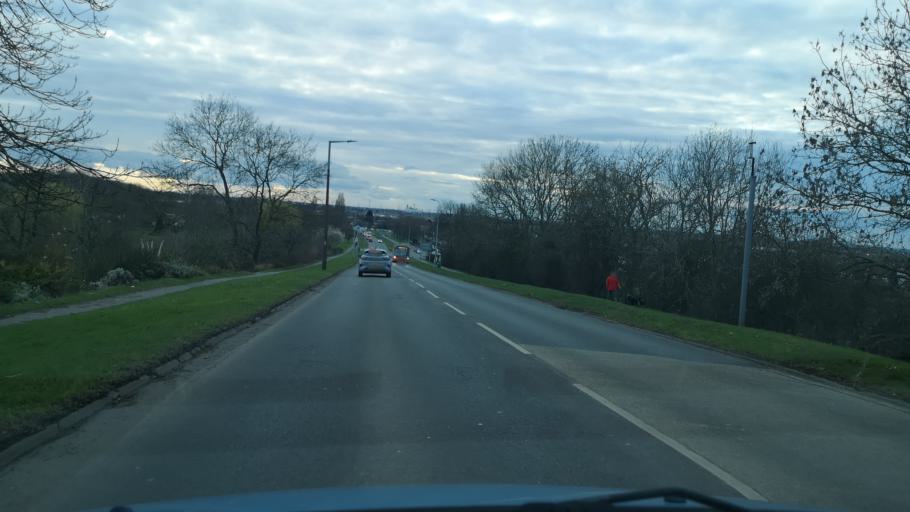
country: GB
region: England
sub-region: North Lincolnshire
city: Scunthorpe
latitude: 53.5900
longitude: -0.6749
